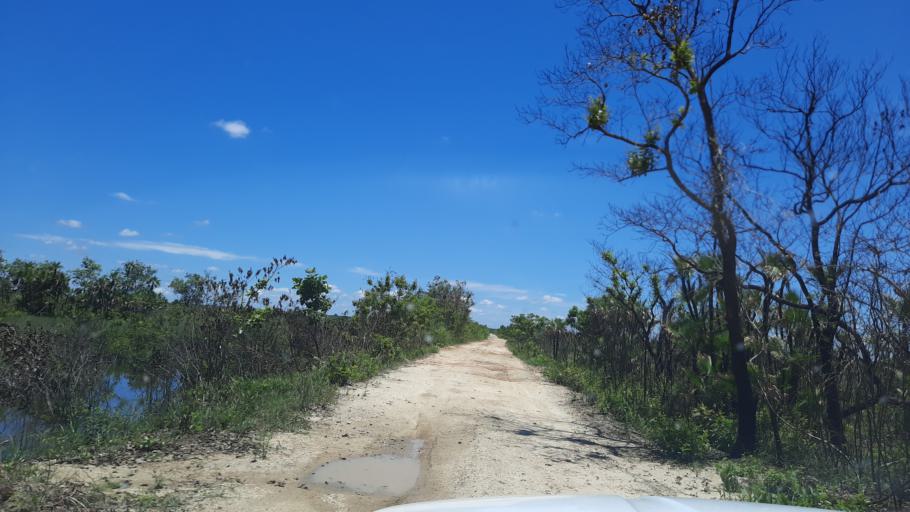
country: BZ
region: Cayo
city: Belmopan
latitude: 17.3778
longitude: -88.4891
